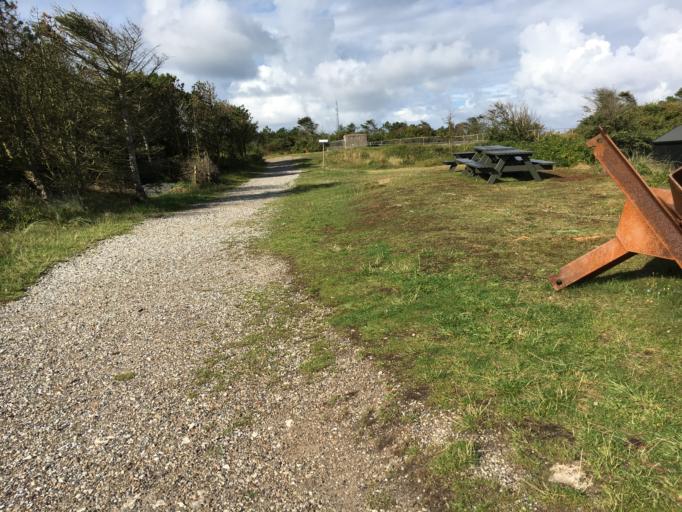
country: DK
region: North Denmark
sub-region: Thisted Kommune
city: Hanstholm
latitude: 57.1205
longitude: 8.6176
